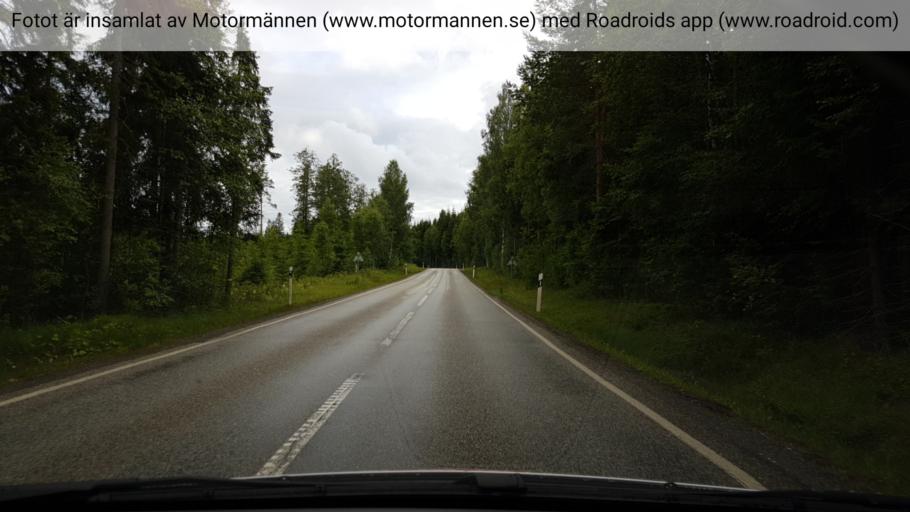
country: SE
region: OErebro
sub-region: Ljusnarsbergs Kommun
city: Kopparberg
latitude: 59.8606
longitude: 15.0030
